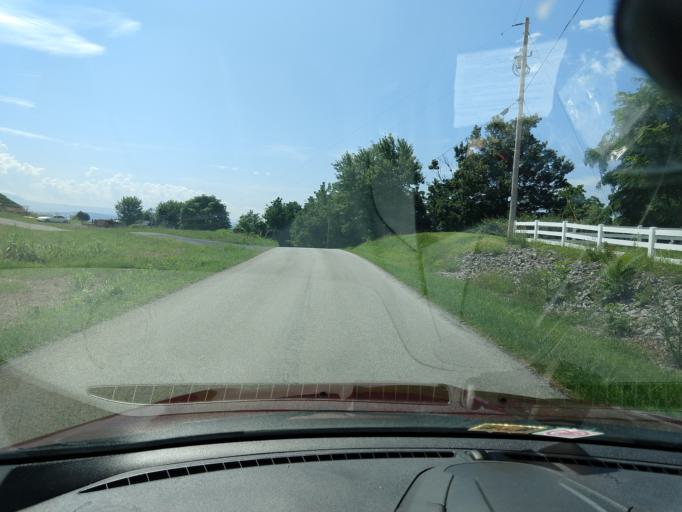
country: US
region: Virginia
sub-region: Rockingham County
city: Broadway
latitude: 38.5727
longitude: -78.8880
